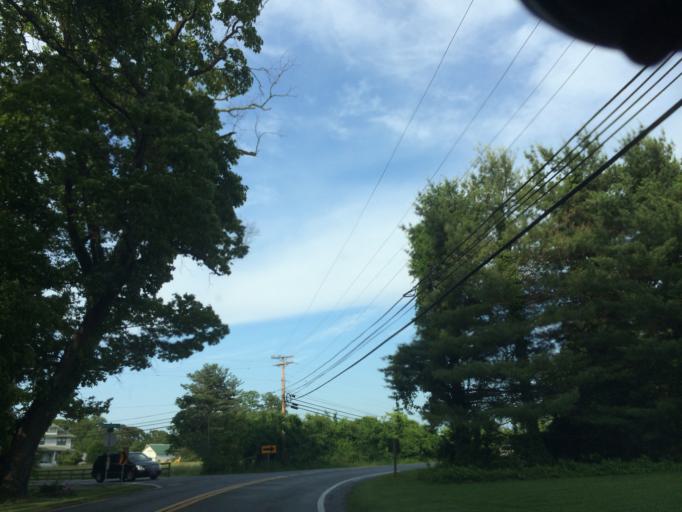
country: US
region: Maryland
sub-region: Carroll County
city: Sykesville
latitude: 39.2837
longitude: -77.0171
